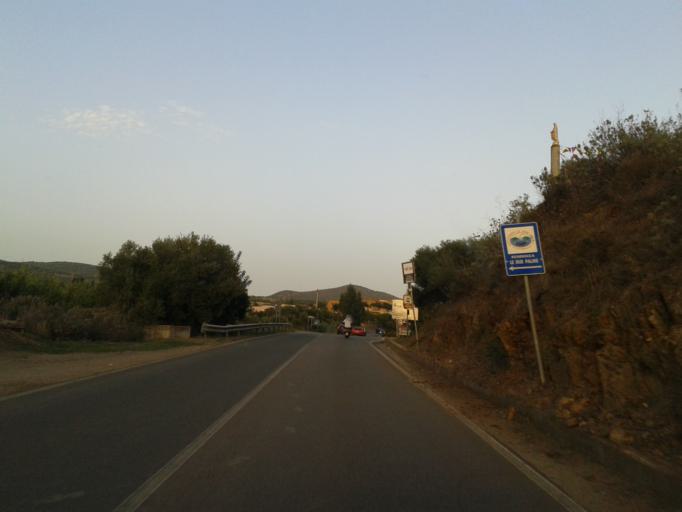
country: IT
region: Sardinia
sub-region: Provincia di Cagliari
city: Villasimius
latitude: 39.1456
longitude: 9.5090
